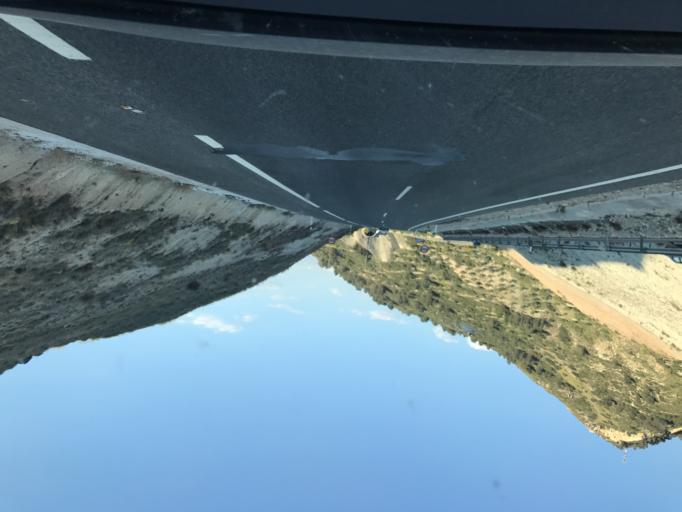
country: ES
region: Andalusia
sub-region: Provincia de Jaen
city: Pegalajar
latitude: 37.6974
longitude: -3.6339
